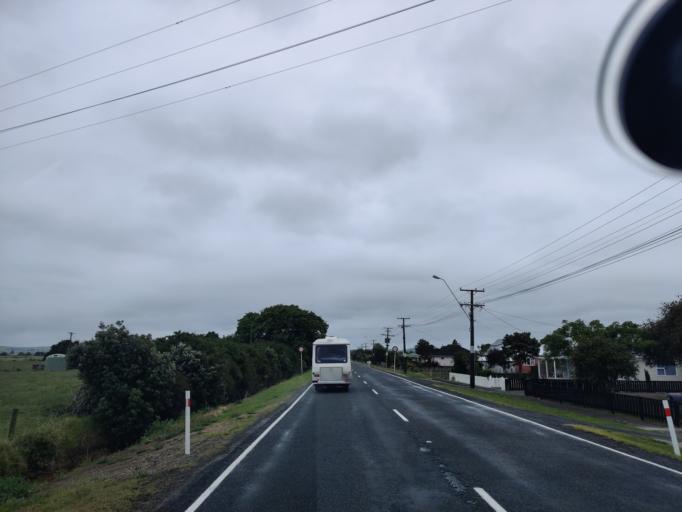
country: NZ
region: Northland
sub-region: Kaipara District
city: Dargaville
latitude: -36.1317
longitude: 174.0320
